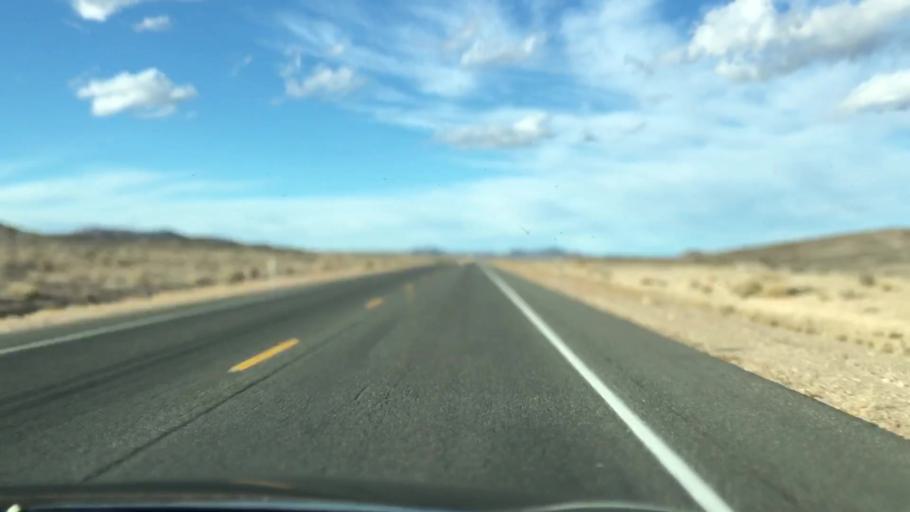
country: US
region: Nevada
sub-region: Esmeralda County
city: Goldfield
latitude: 37.5343
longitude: -117.1934
